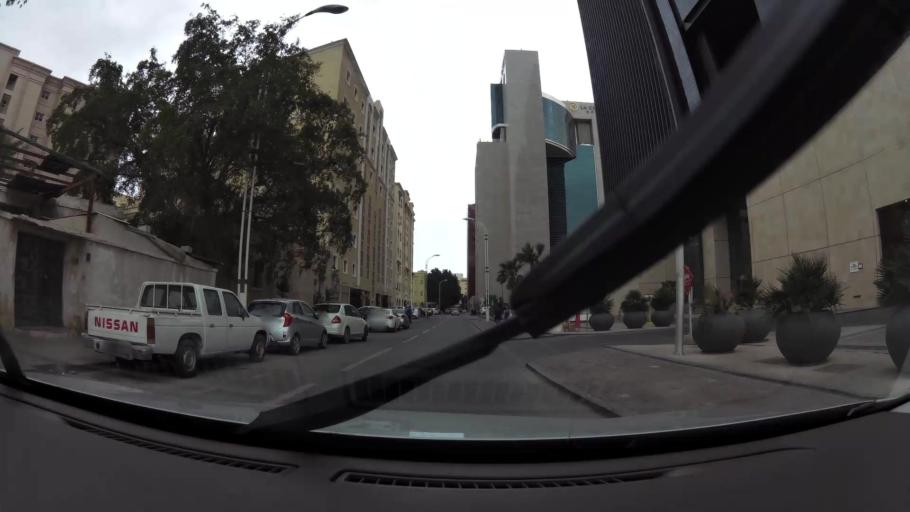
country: QA
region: Baladiyat ad Dawhah
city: Doha
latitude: 25.2817
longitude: 51.5078
